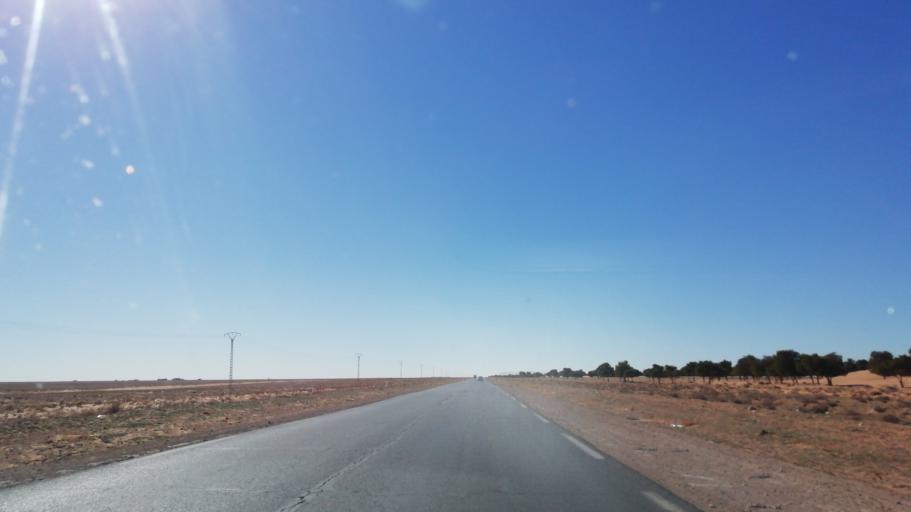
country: DZ
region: Saida
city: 'Ain el Hadjar
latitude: 33.9956
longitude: 0.0395
